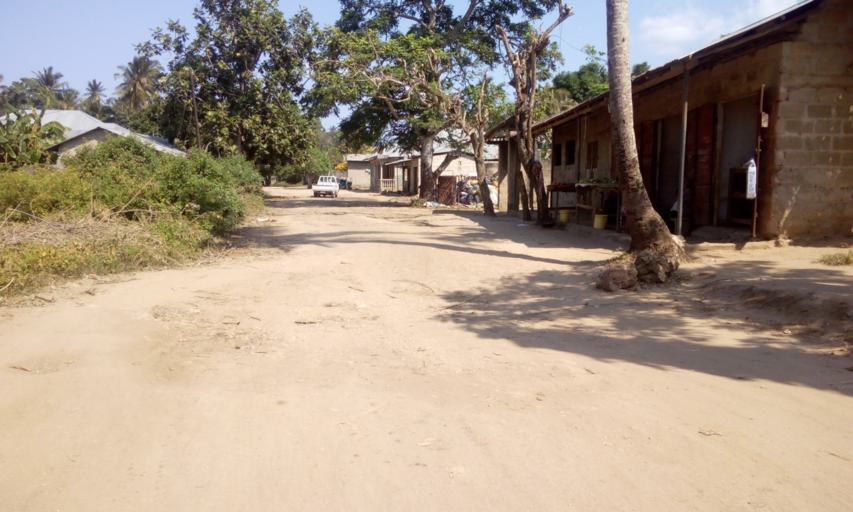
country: TZ
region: Zanzibar Central/South
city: Koani
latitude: -6.2003
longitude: 39.2631
